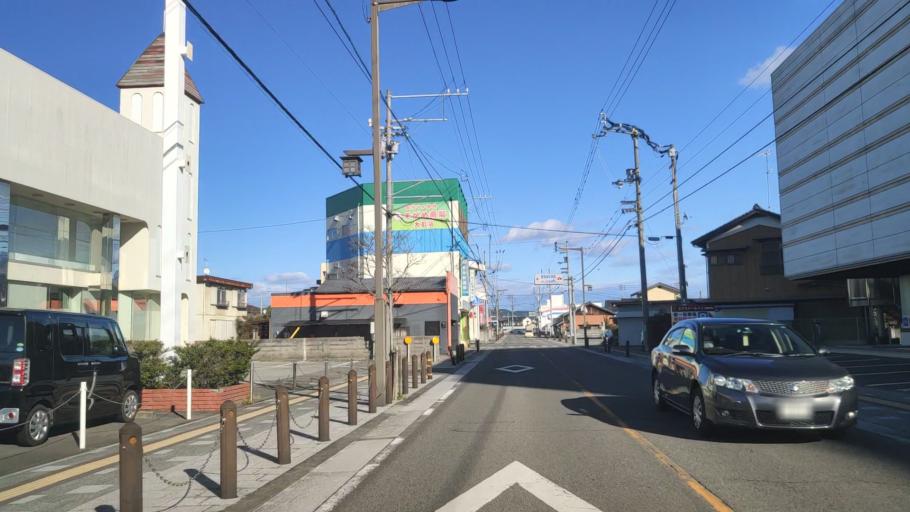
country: JP
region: Ehime
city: Saijo
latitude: 33.9139
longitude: 133.1897
